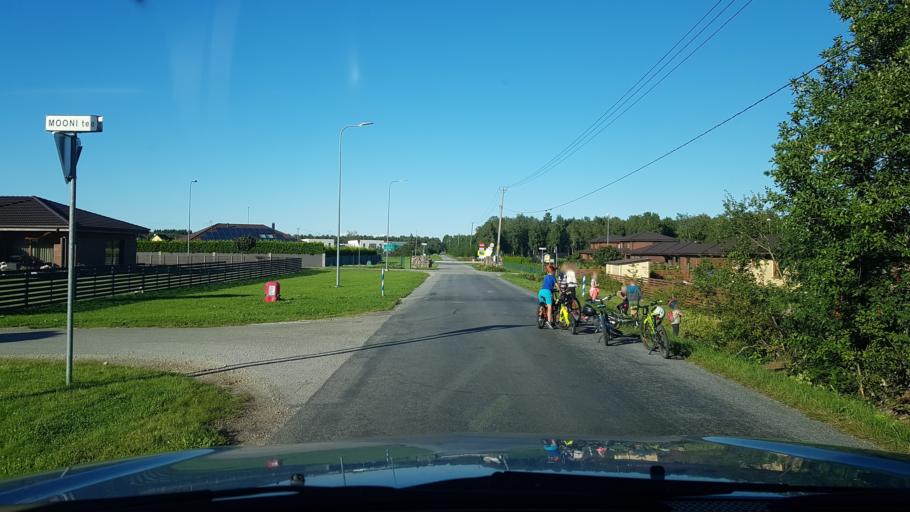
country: EE
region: Harju
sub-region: Rae vald
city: Jueri
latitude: 59.3892
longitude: 24.8536
